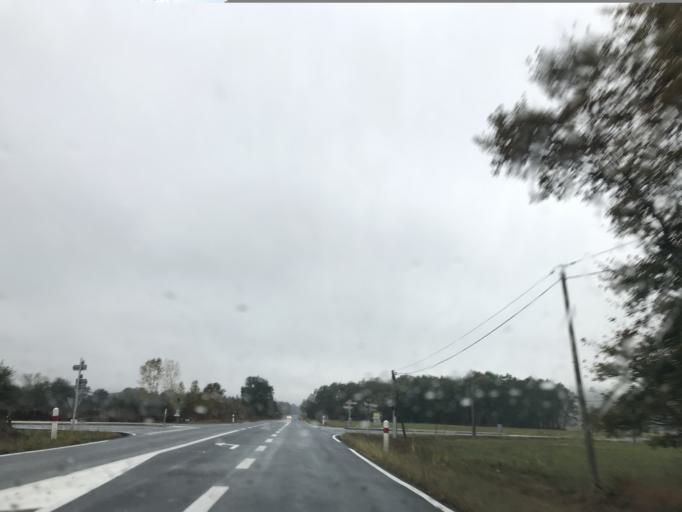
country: FR
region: Auvergne
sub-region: Departement du Puy-de-Dome
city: Lezoux
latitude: 45.7802
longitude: 3.4369
